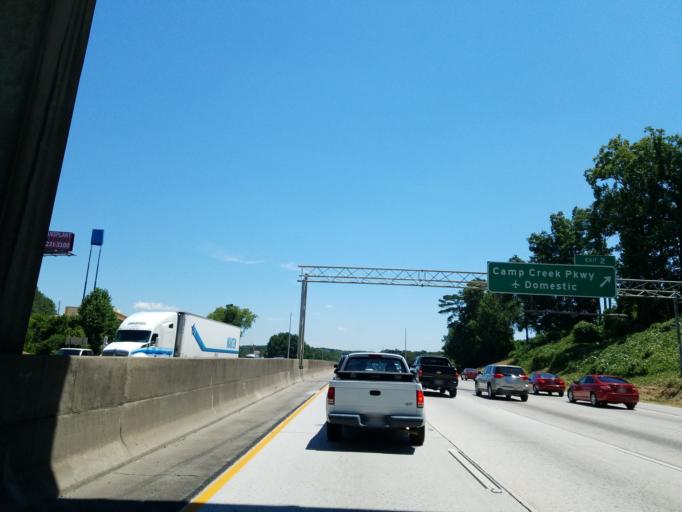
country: US
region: Georgia
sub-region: Fulton County
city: College Park
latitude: 33.6608
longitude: -84.4977
